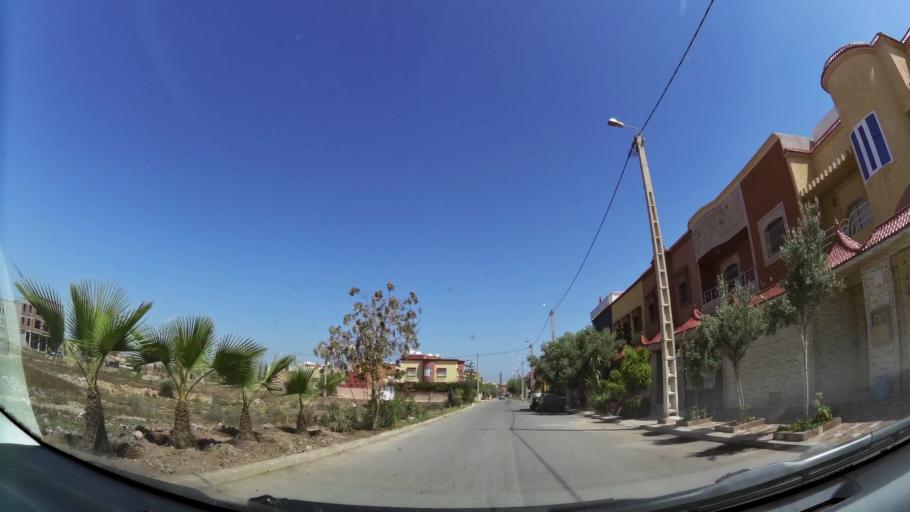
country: MA
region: Souss-Massa-Draa
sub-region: Inezgane-Ait Mellou
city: Inezgane
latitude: 30.3215
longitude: -9.5060
